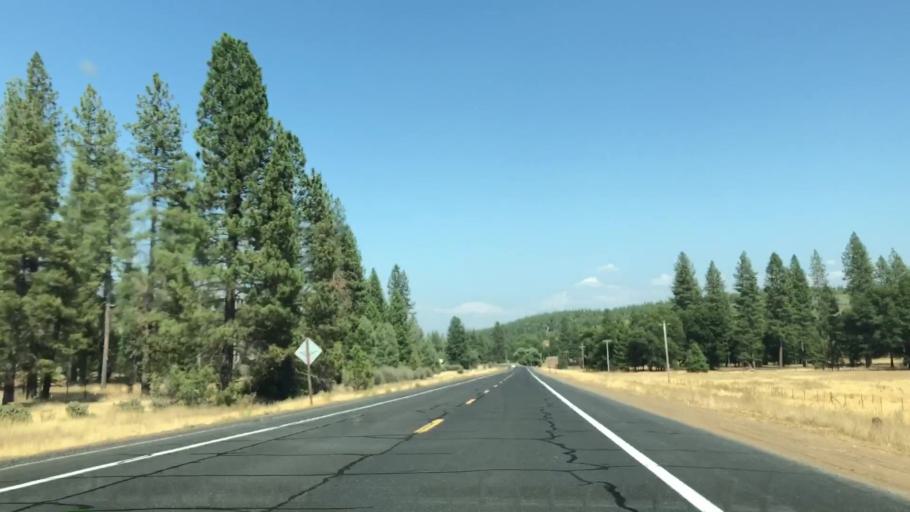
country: US
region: California
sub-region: Tuolumne County
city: Tuolumne City
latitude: 37.8145
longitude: -120.1158
